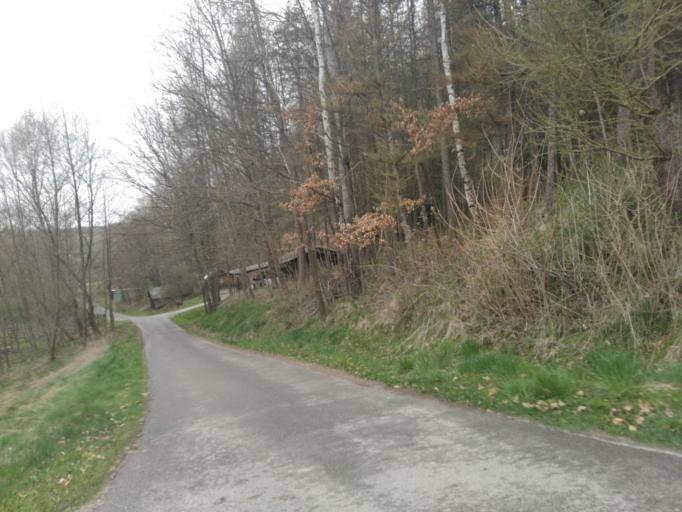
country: PL
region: Subcarpathian Voivodeship
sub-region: Powiat strzyzowski
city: Wysoka Strzyzowska
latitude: 49.8860
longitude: 21.7208
